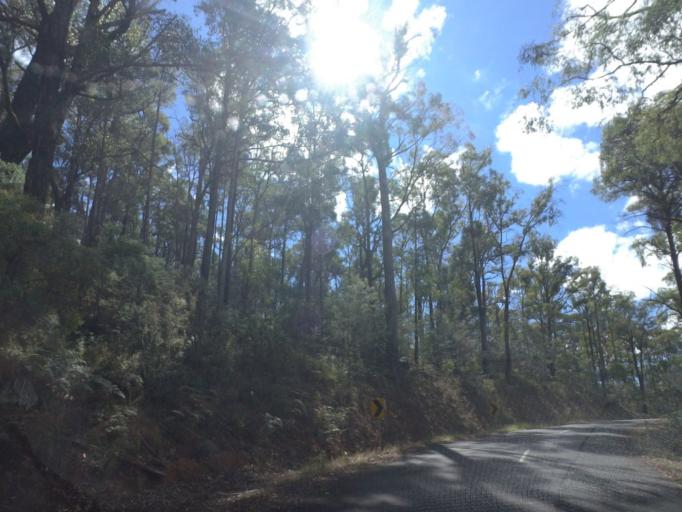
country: AU
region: Victoria
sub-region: Murrindindi
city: Alexandra
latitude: -37.3346
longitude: 145.9449
